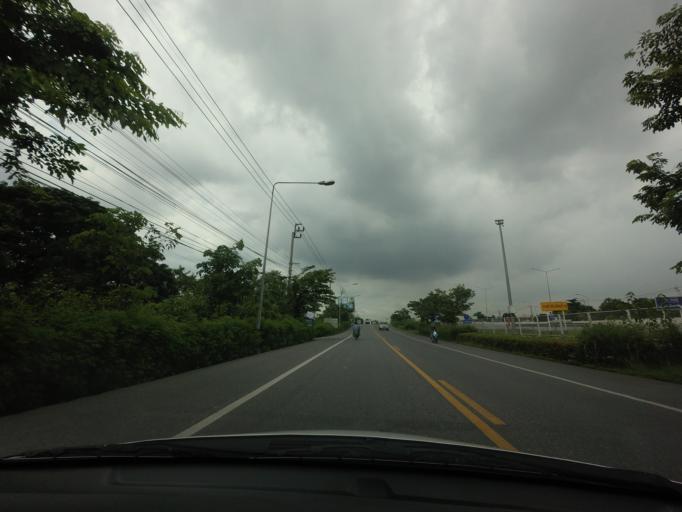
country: TH
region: Bangkok
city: Saphan Sung
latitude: 13.7587
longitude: 100.6972
